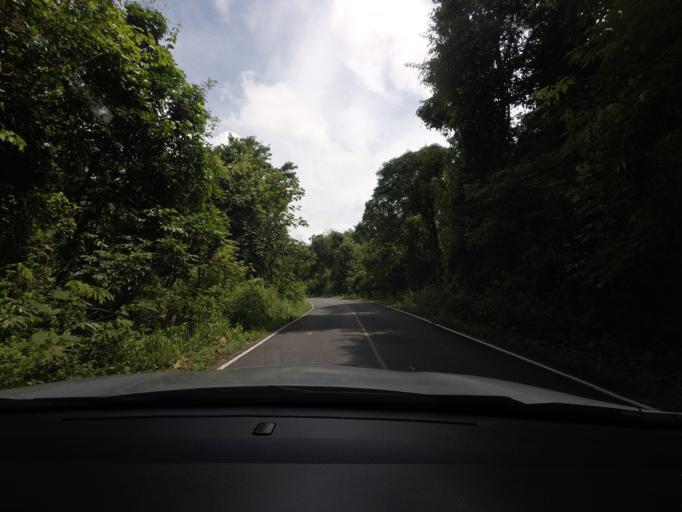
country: TH
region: Nakhon Nayok
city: Pak Phli
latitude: 14.2965
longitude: 101.3933
